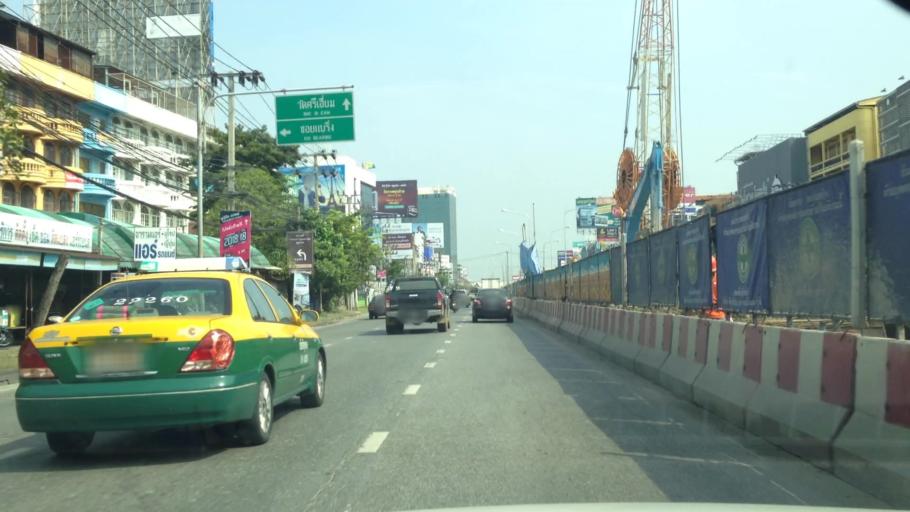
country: TH
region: Bangkok
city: Bang Na
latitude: 13.6430
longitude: 100.6358
